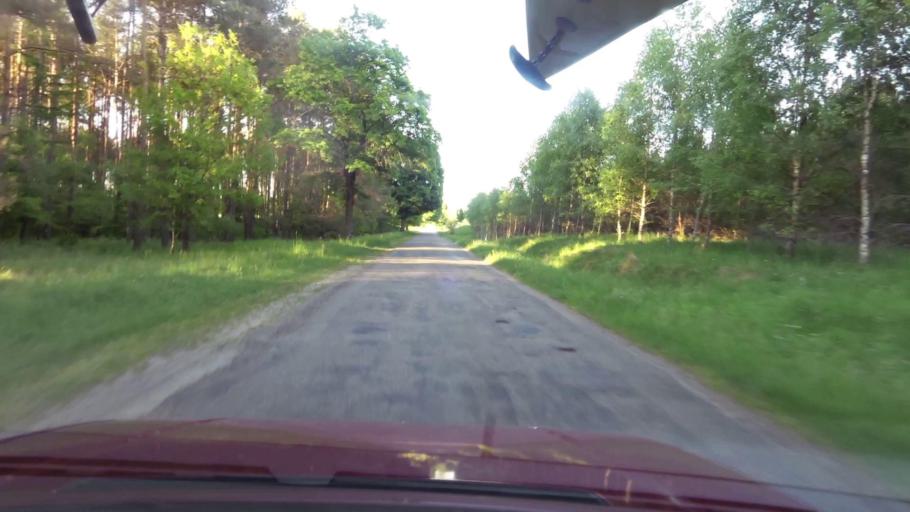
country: PL
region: West Pomeranian Voivodeship
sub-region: Powiat szczecinecki
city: Bialy Bor
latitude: 53.9423
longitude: 16.7646
